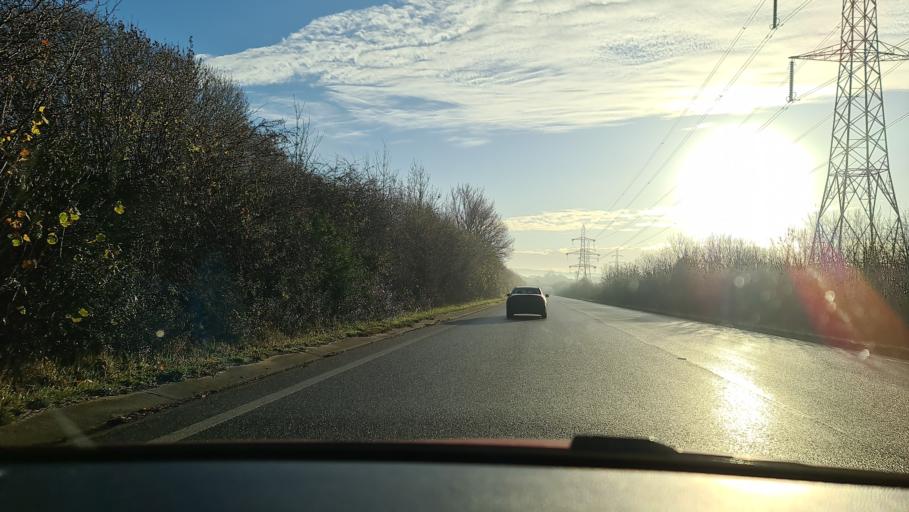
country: GB
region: England
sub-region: Buckinghamshire
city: Wendover
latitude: 51.7647
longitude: -0.7539
